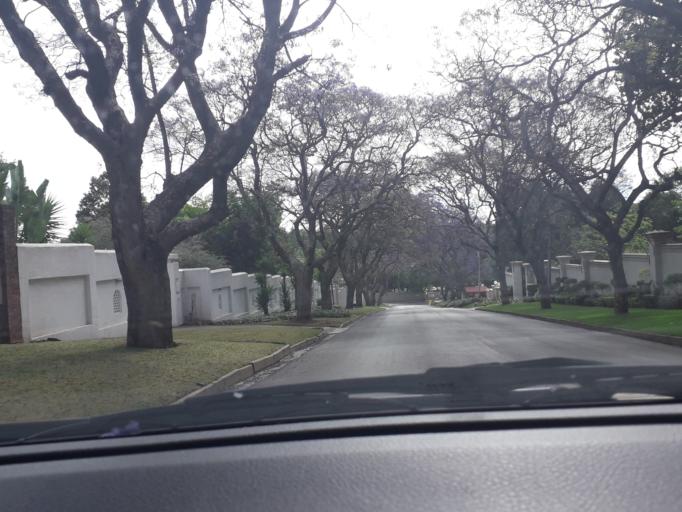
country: ZA
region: Gauteng
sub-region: City of Johannesburg Metropolitan Municipality
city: Johannesburg
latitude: -26.1584
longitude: 28.0601
